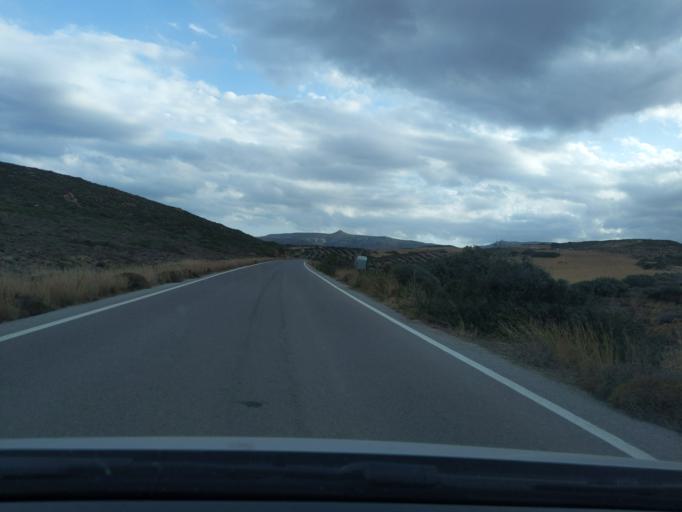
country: GR
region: Crete
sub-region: Nomos Lasithiou
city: Palekastro
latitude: 35.2341
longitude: 26.2521
